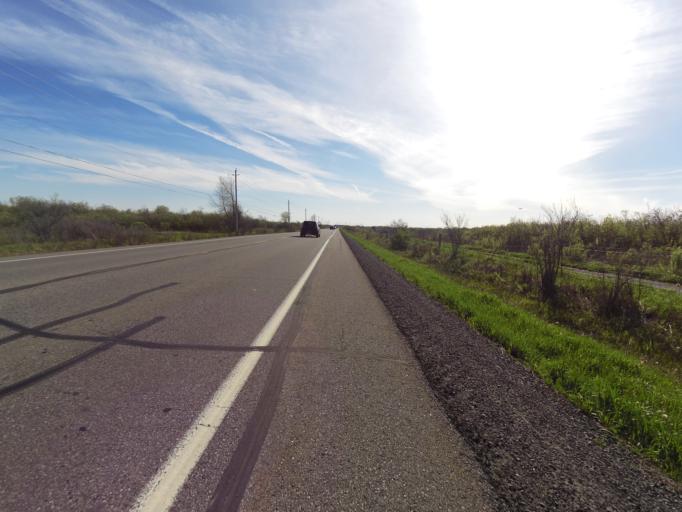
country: CA
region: Ontario
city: Ottawa
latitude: 45.3026
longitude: -75.6655
